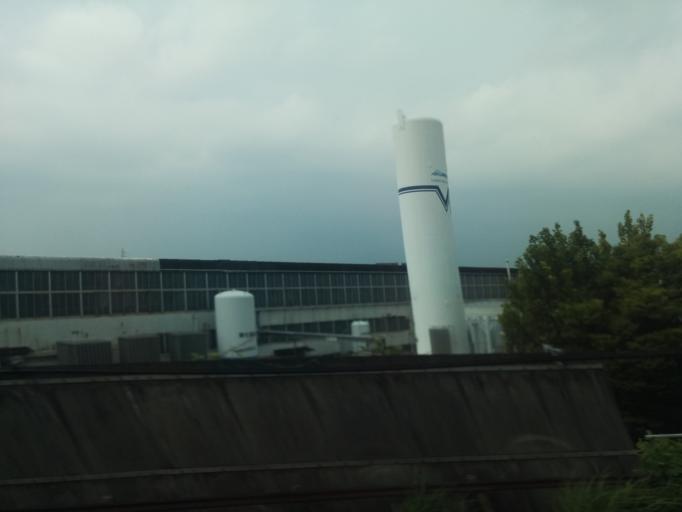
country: JP
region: Aichi
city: Chiryu
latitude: 35.0100
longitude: 137.0079
